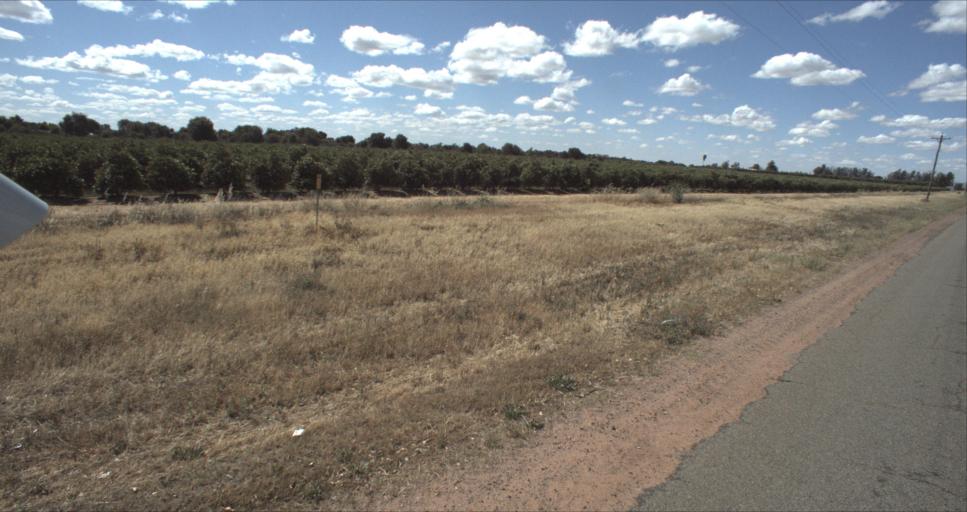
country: AU
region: New South Wales
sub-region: Leeton
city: Leeton
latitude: -34.5161
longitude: 146.2372
